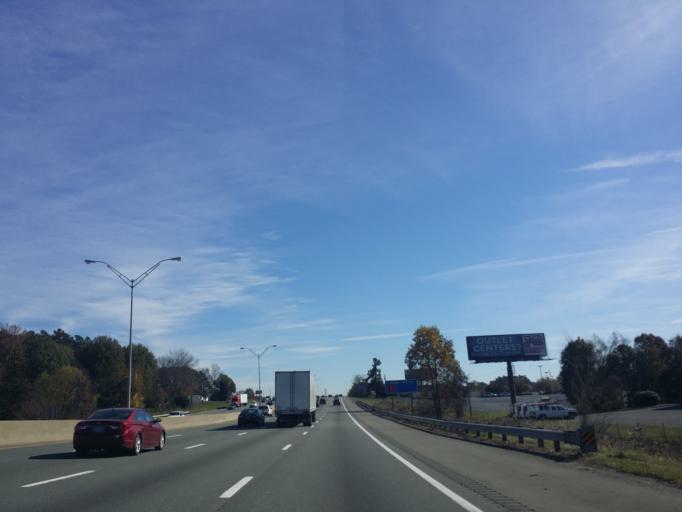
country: US
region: North Carolina
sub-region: Alamance County
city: Elon
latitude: 36.0686
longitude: -79.4801
